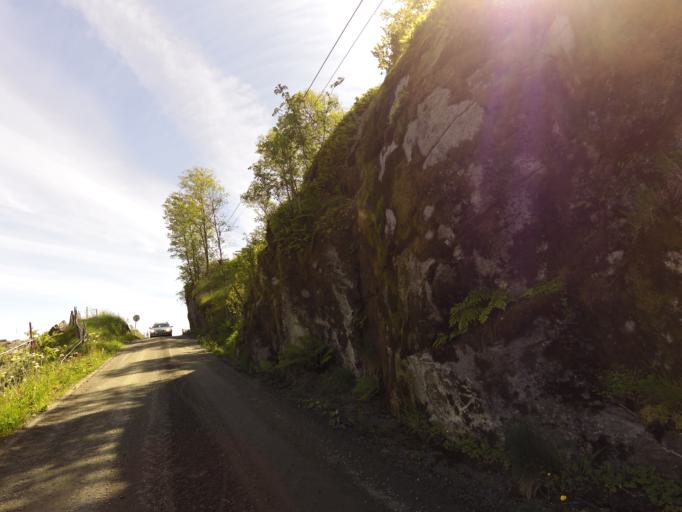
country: NO
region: Rogaland
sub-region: Sokndal
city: Hauge i Dalane
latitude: 58.3572
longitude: 6.1541
